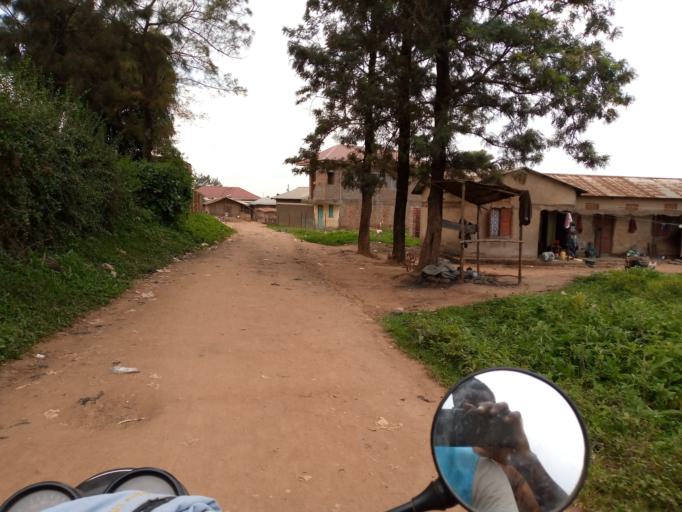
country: UG
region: Eastern Region
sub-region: Mbale District
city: Mbale
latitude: 1.0852
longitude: 34.1689
